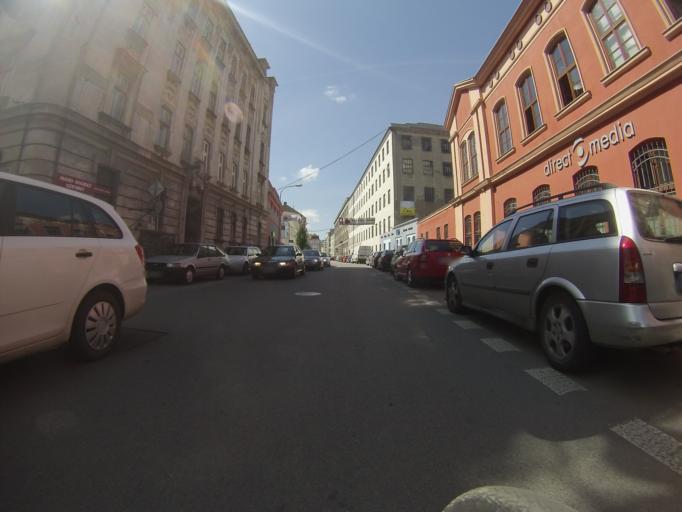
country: CZ
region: South Moravian
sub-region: Mesto Brno
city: Brno
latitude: 49.1939
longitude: 16.6220
